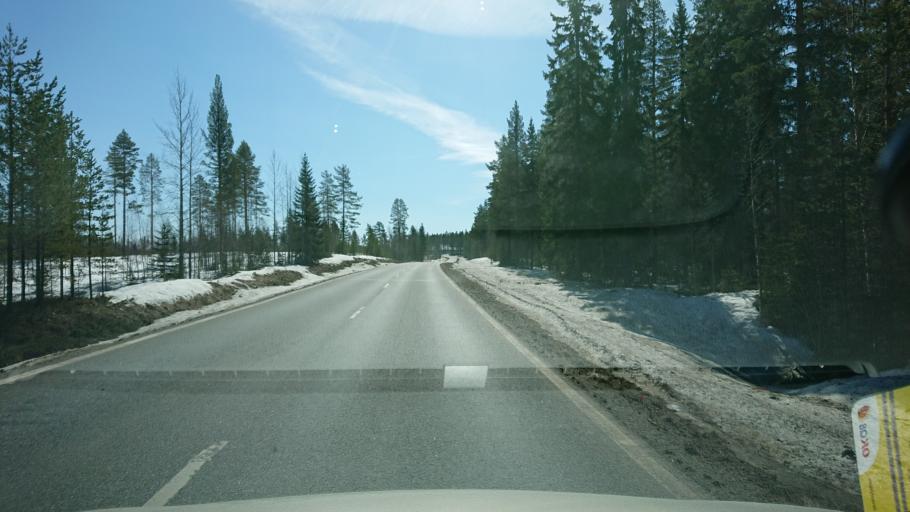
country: SE
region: Vaesterbotten
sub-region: Dorotea Kommun
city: Dorotea
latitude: 64.0301
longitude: 16.2709
